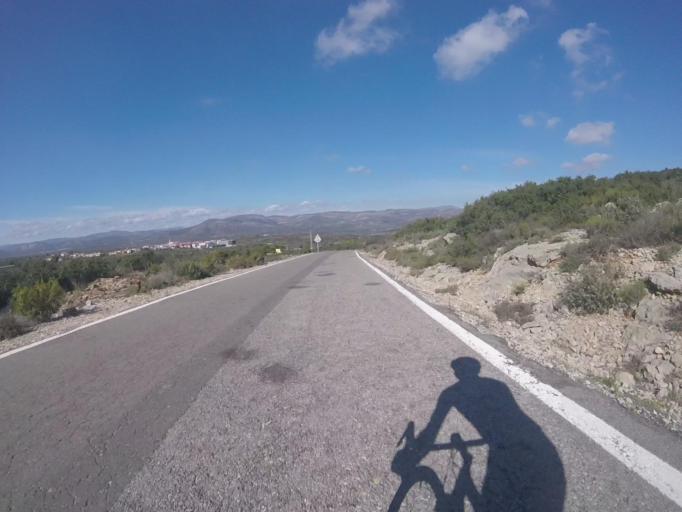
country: ES
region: Valencia
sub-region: Provincia de Castello
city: Albocasser
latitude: 40.3555
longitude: 0.0392
